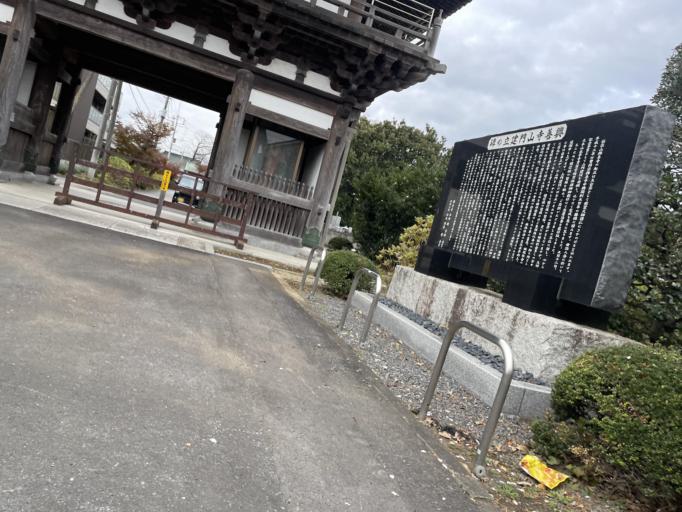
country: JP
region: Saitama
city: Shiraoka
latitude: 36.0225
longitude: 139.6594
